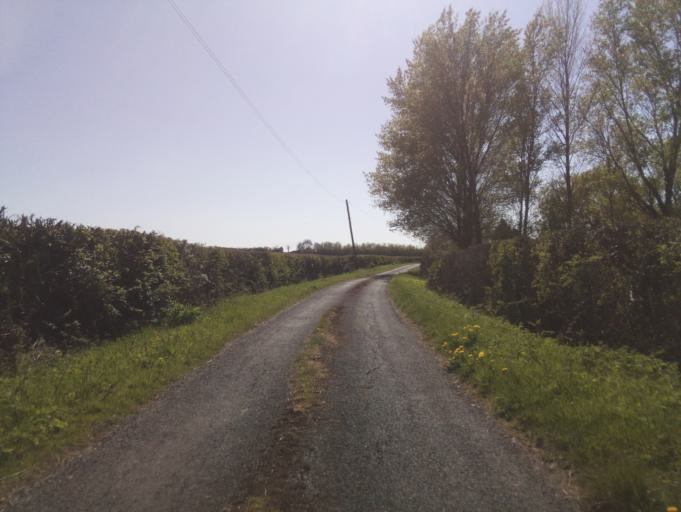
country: GB
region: England
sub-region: Gloucestershire
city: Berkeley
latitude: 51.6661
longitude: -2.4335
